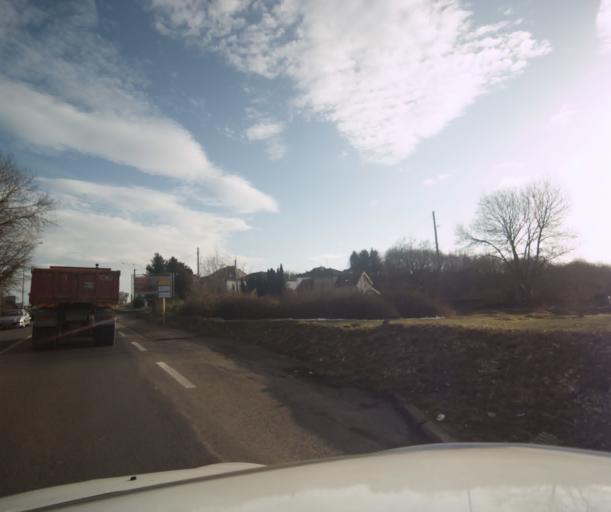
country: FR
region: Franche-Comte
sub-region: Departement du Doubs
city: Besancon
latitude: 47.2606
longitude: 6.0078
